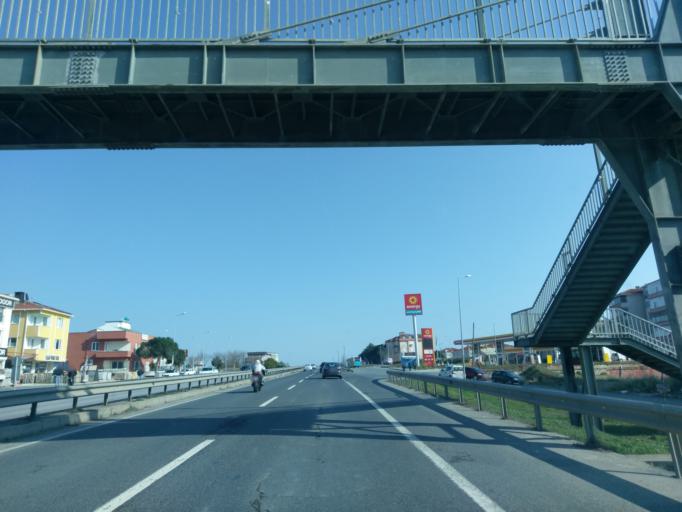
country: TR
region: Istanbul
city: Selimpasa
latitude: 41.0505
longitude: 28.3897
